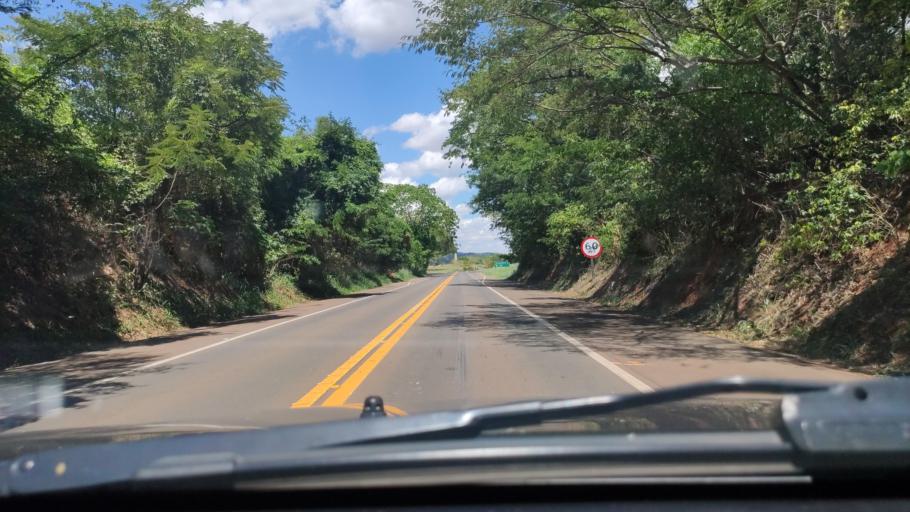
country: BR
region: Sao Paulo
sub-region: Boa Esperanca Do Sul
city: Boa Esperanca do Sul
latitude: -22.0698
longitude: -48.4287
